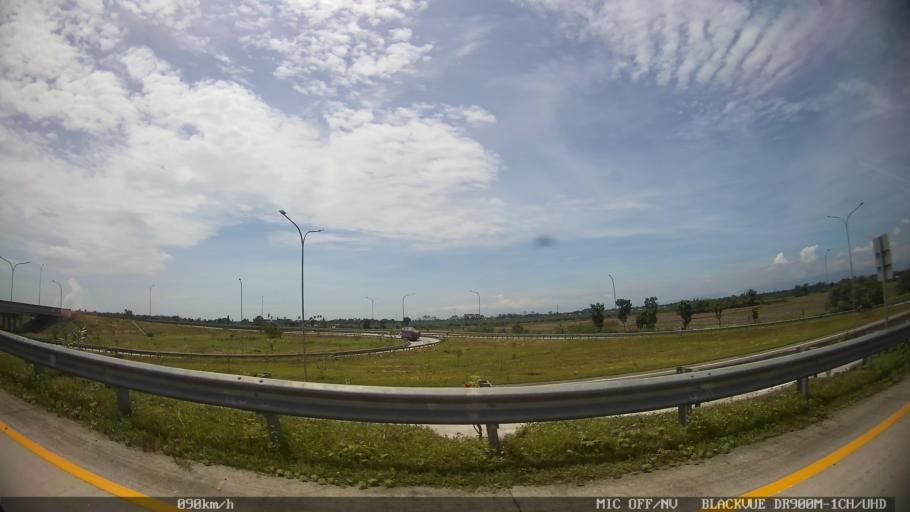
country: ID
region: North Sumatra
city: Perbaungan
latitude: 3.5321
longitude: 98.8917
